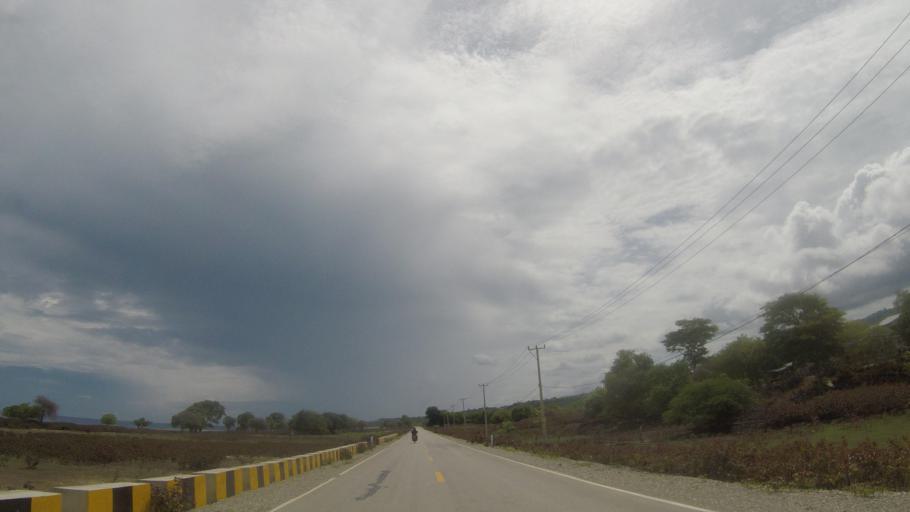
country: TL
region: Baucau
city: Baucau
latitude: -8.4542
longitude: 126.6279
